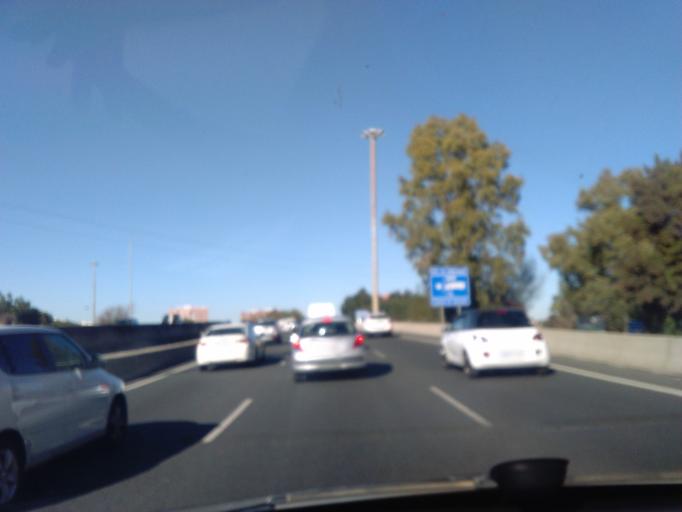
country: ES
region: Andalusia
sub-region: Provincia de Sevilla
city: Sevilla
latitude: 37.3987
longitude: -5.9450
